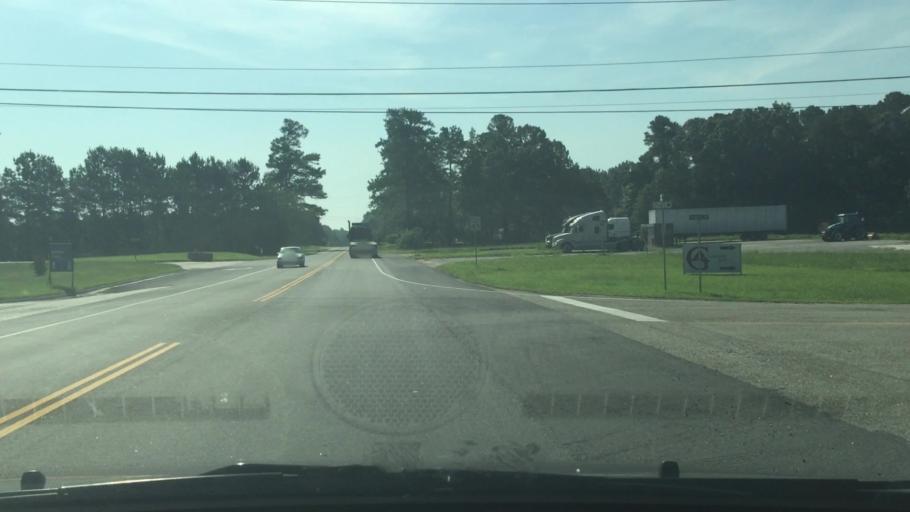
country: US
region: Virginia
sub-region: City of Petersburg
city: Petersburg
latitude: 37.0801
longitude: -77.3561
